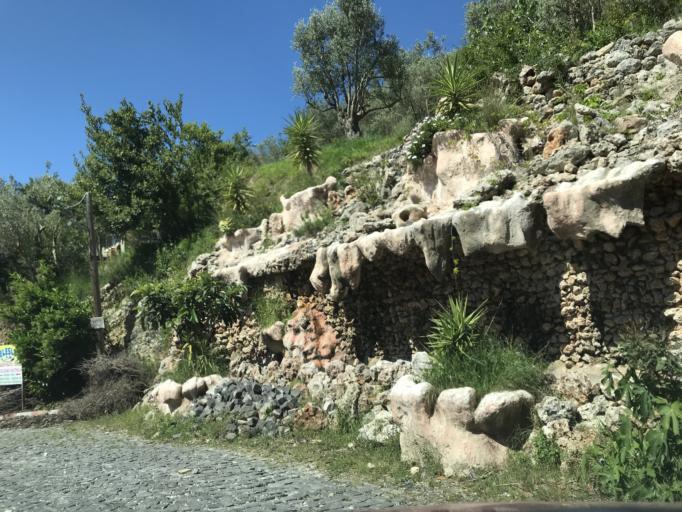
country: TR
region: Hatay
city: Samandag
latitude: 36.1326
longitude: 35.9740
